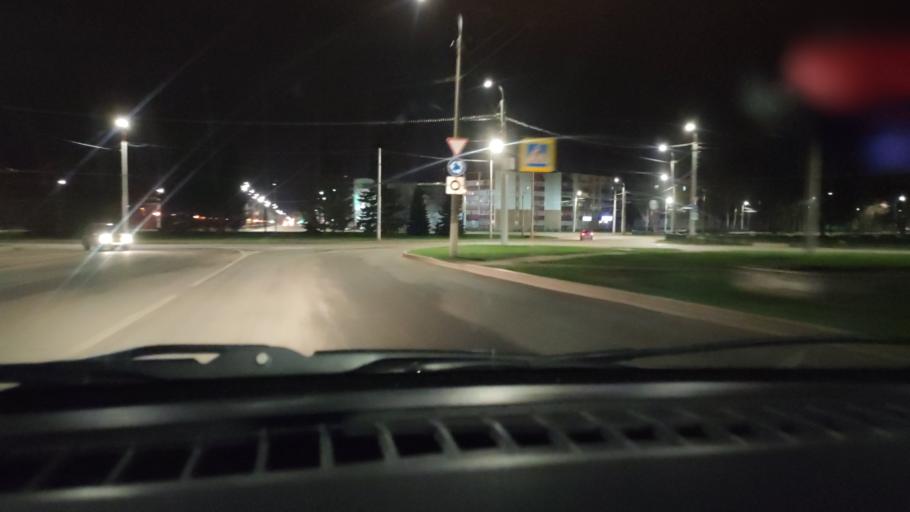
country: RU
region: Bashkortostan
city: Sterlitamak
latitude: 53.6382
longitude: 55.9084
